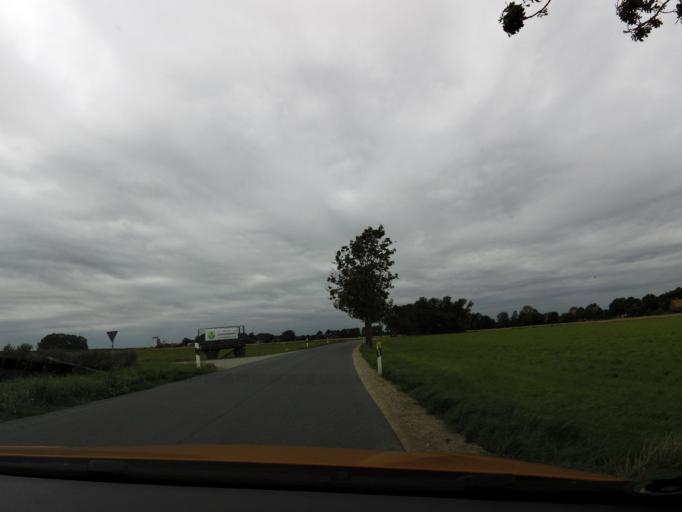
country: DE
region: Lower Saxony
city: Wirdum
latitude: 53.5039
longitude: 7.1590
